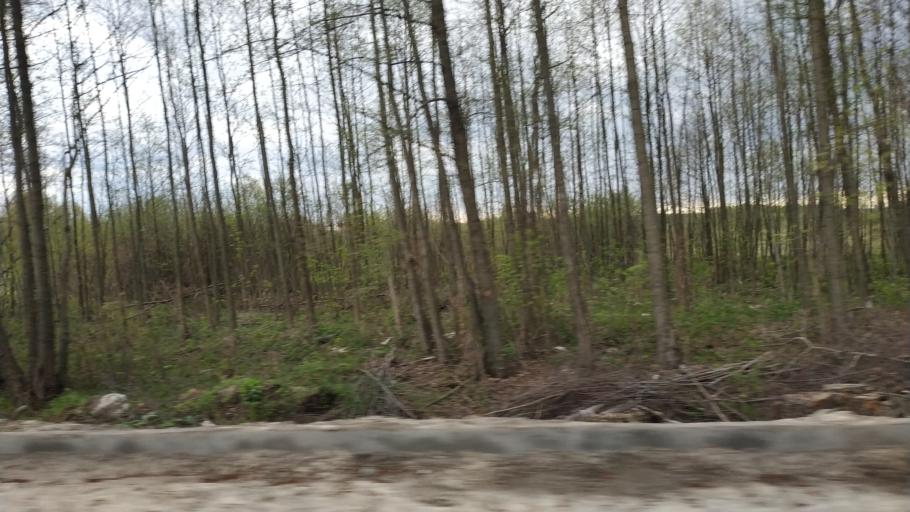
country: RU
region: Moskovskaya
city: Pavlovskiy Posad
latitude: 55.7984
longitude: 38.6874
